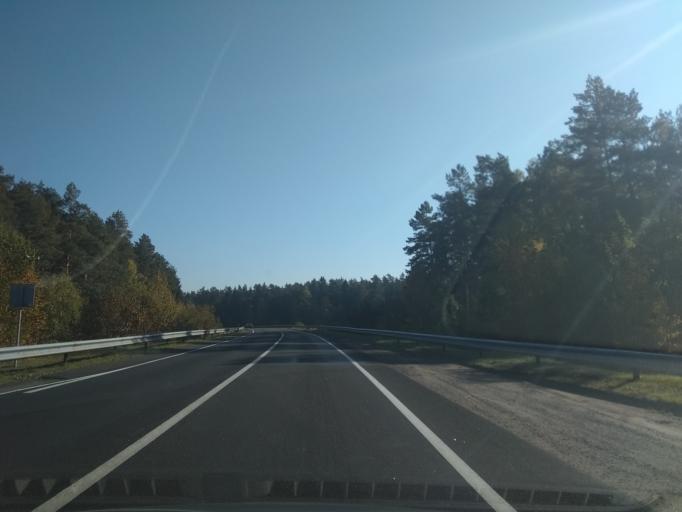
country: BY
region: Brest
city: Baranovichi
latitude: 53.0480
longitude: 25.8453
